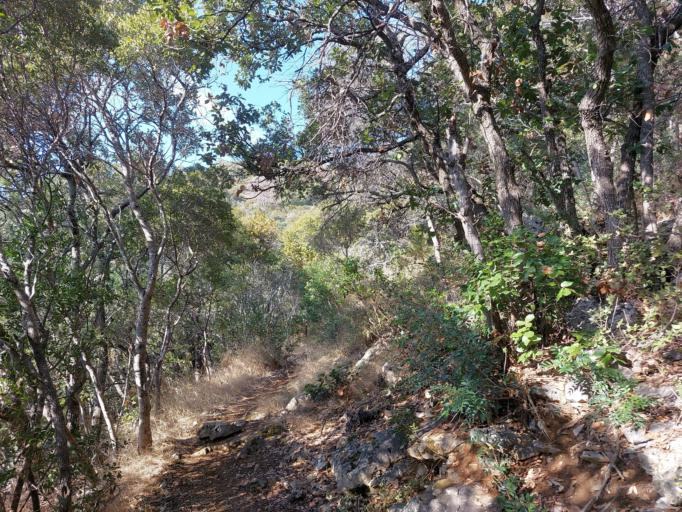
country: HR
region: Dubrovacko-Neretvanska
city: Smokvica
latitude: 42.7664
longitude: 16.8030
